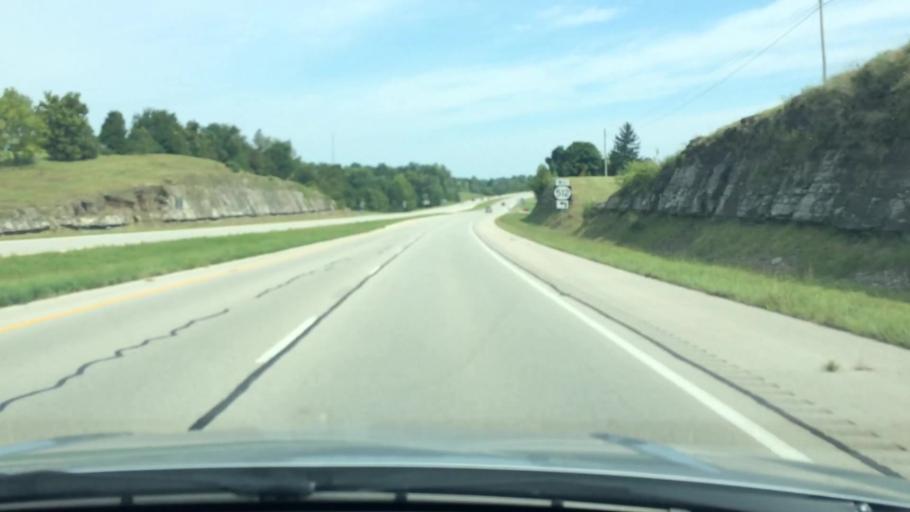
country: US
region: Kentucky
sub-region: Anderson County
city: Lawrenceburg
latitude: 38.0961
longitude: -84.9196
